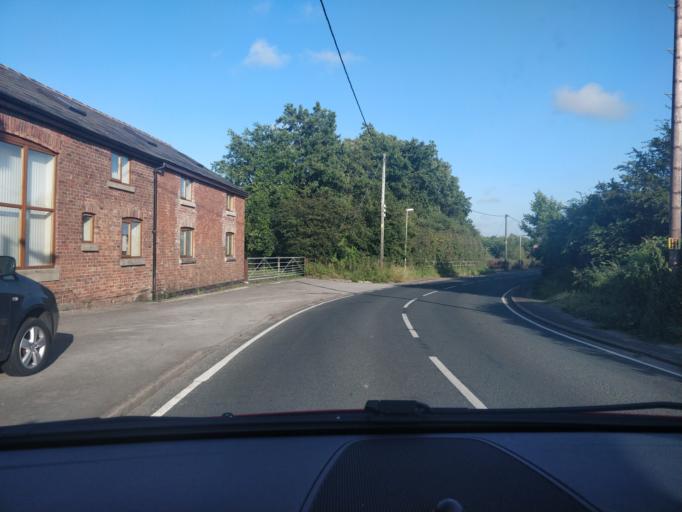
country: GB
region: England
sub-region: Lancashire
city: Tarleton
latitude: 53.6439
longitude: -2.8518
